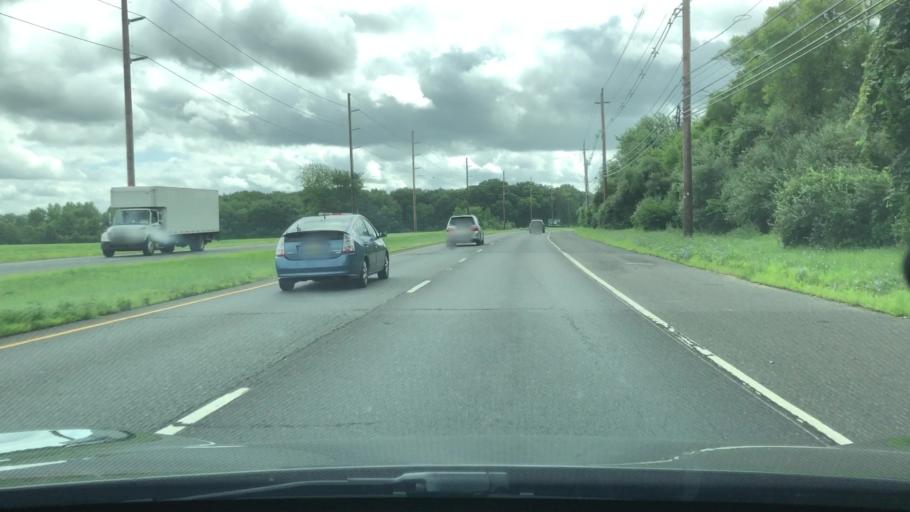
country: US
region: New Jersey
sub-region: Mercer County
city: Twin Rivers
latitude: 40.2663
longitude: -74.4601
